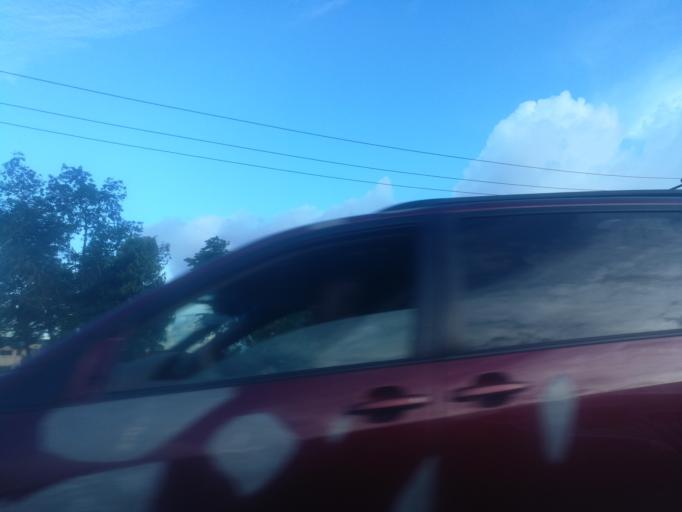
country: NG
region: Lagos
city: Ikeja
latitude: 6.6281
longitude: 3.3638
